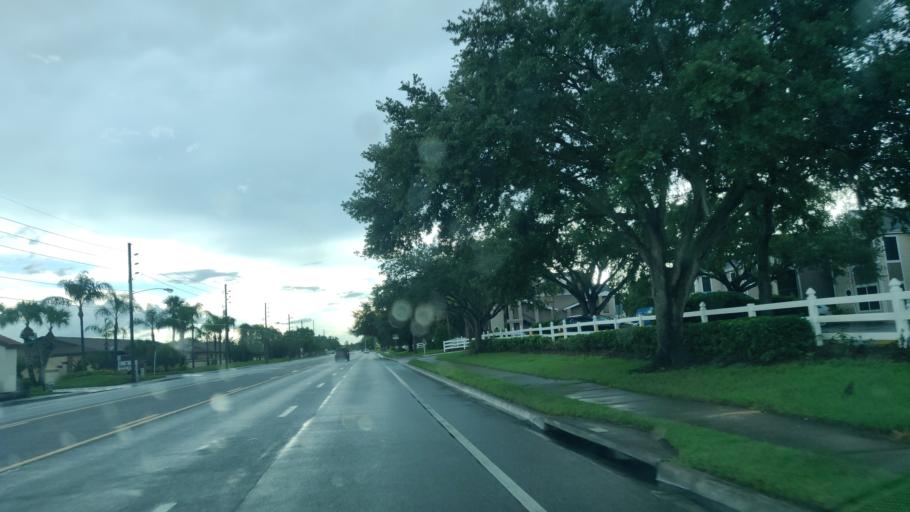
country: US
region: Florida
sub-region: Osceola County
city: Kissimmee
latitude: 28.3093
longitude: -81.4242
